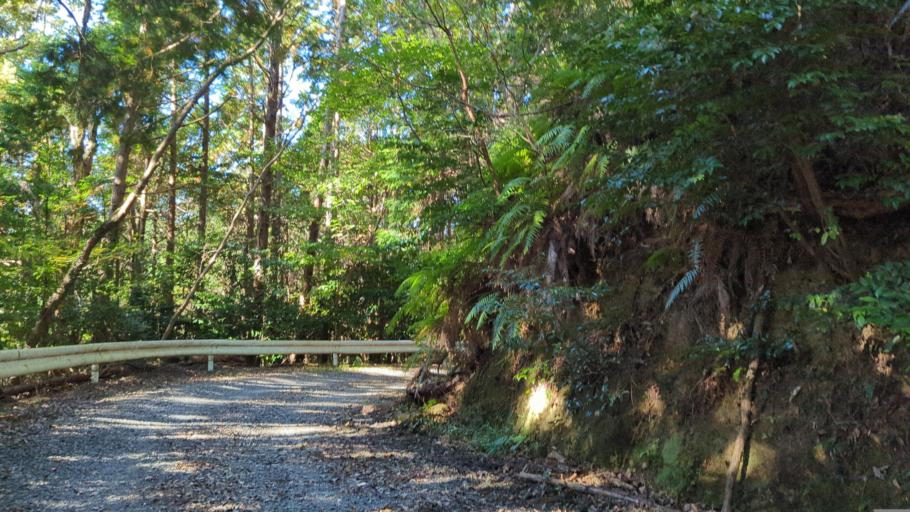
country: JP
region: Aichi
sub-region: Tokai-shi
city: Toyokawa
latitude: 34.7849
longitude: 137.4766
